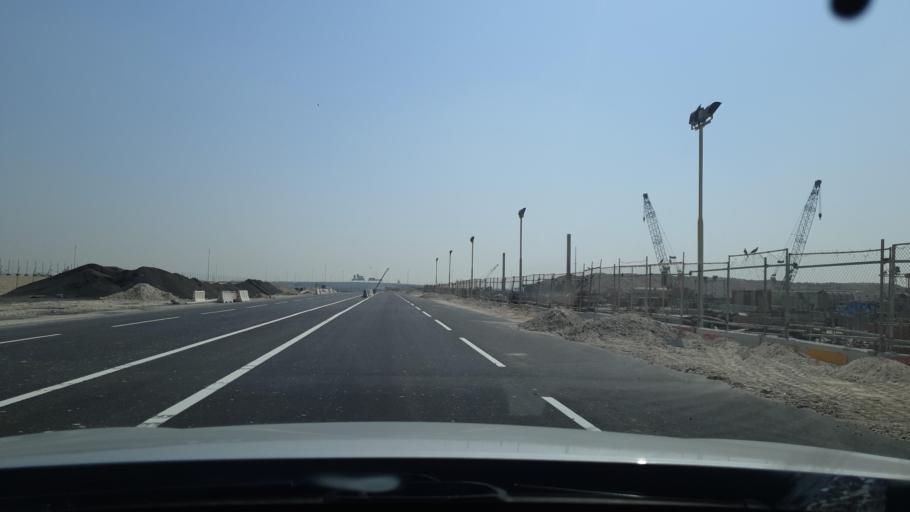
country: QA
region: Baladiyat ad Dawhah
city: Doha
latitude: 25.2243
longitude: 51.5224
